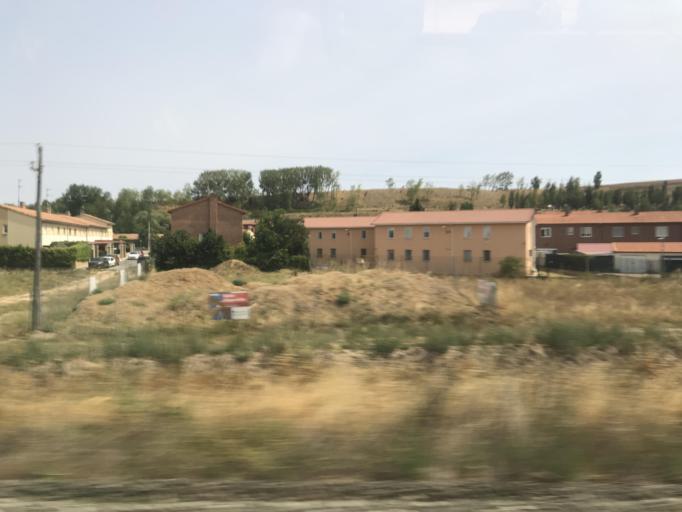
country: ES
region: Castille and Leon
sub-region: Provincia de Burgos
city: Buniel
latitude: 42.3081
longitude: -3.8264
